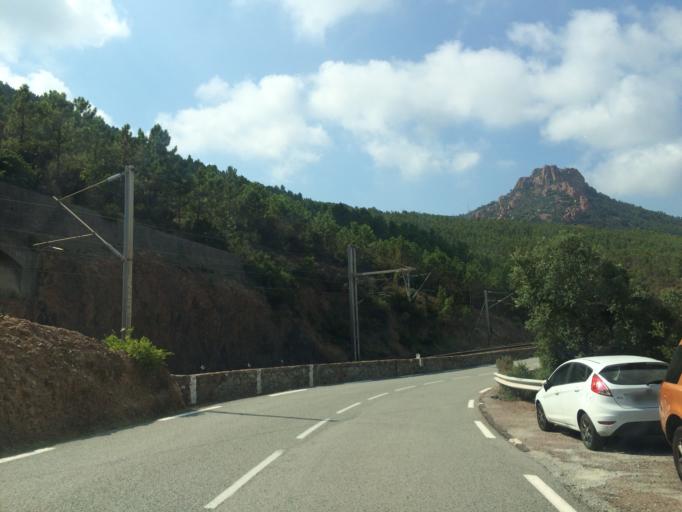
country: FR
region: Provence-Alpes-Cote d'Azur
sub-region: Departement des Alpes-Maritimes
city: Theoule-sur-Mer
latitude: 43.4567
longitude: 6.9199
